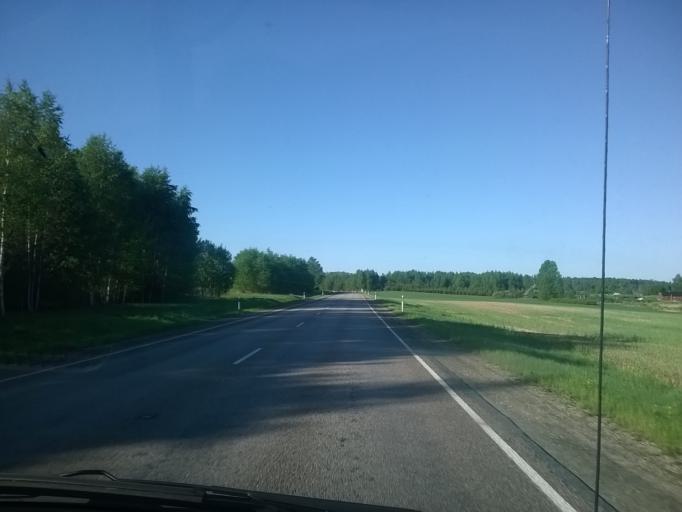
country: EE
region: Valgamaa
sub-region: Torva linn
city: Torva
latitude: 58.0222
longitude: 26.1663
